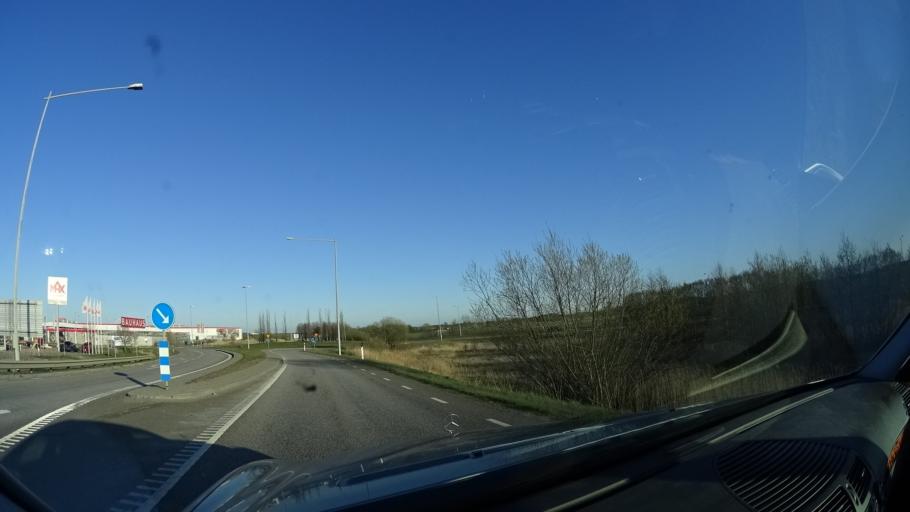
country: SE
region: Skane
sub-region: Helsingborg
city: Hyllinge
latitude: 56.0994
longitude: 12.8506
